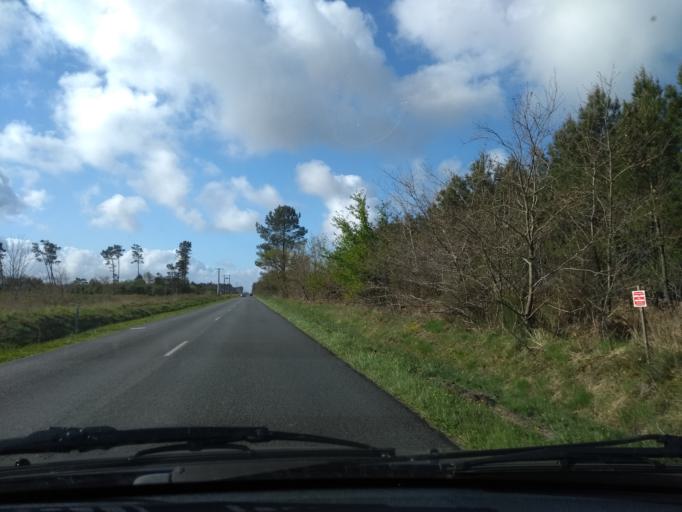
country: FR
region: Aquitaine
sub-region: Departement des Landes
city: Sanguinet
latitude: 44.4504
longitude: -1.0709
